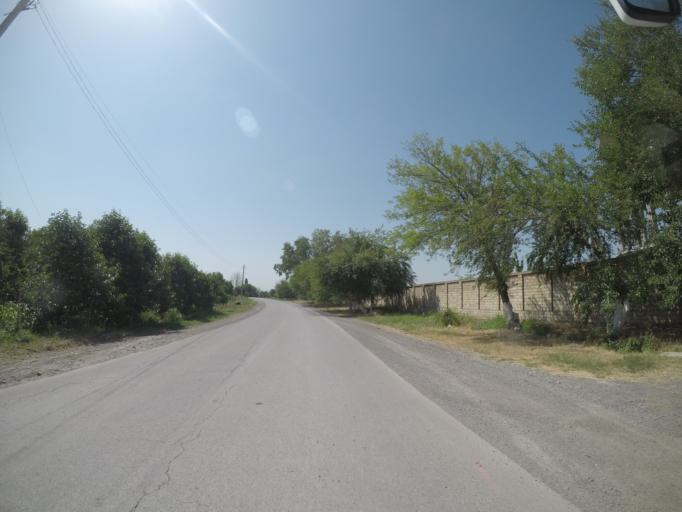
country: AZ
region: Agdas
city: Agdas
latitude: 40.7055
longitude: 47.5395
